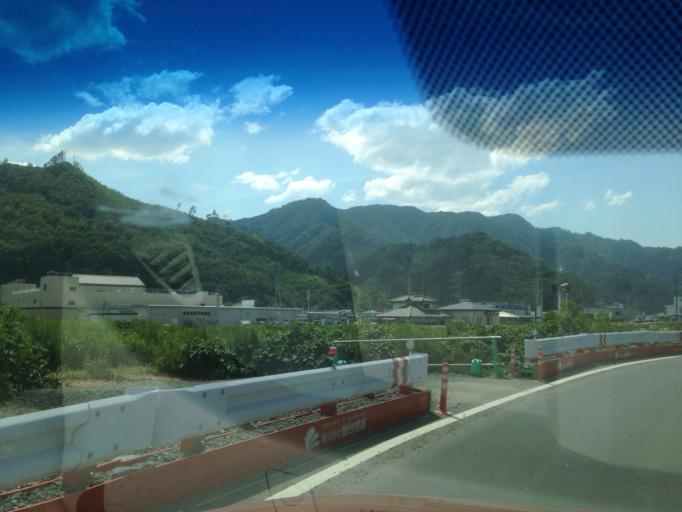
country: JP
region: Iwate
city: Otsuchi
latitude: 39.3557
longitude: 141.8968
